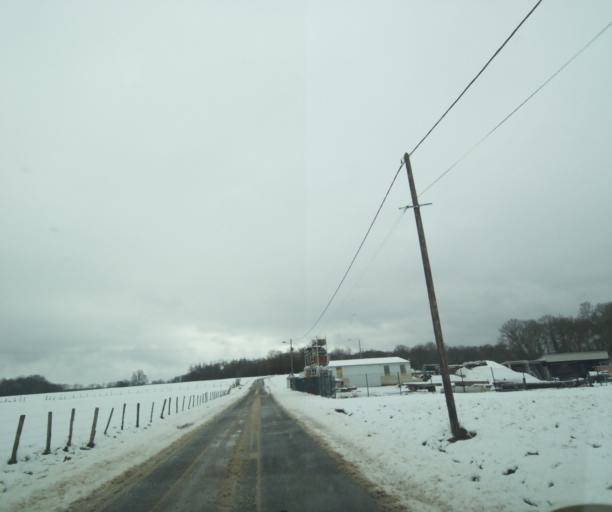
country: FR
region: Champagne-Ardenne
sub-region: Departement de la Haute-Marne
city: Montier-en-Der
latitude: 48.4293
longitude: 4.7283
